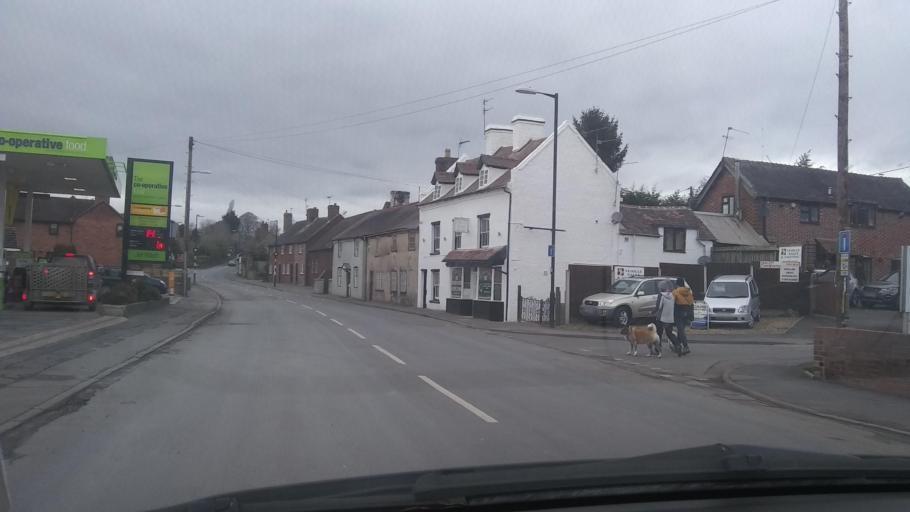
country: GB
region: England
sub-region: Shropshire
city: Cleobury Mortimer
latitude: 52.3785
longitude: -2.4843
